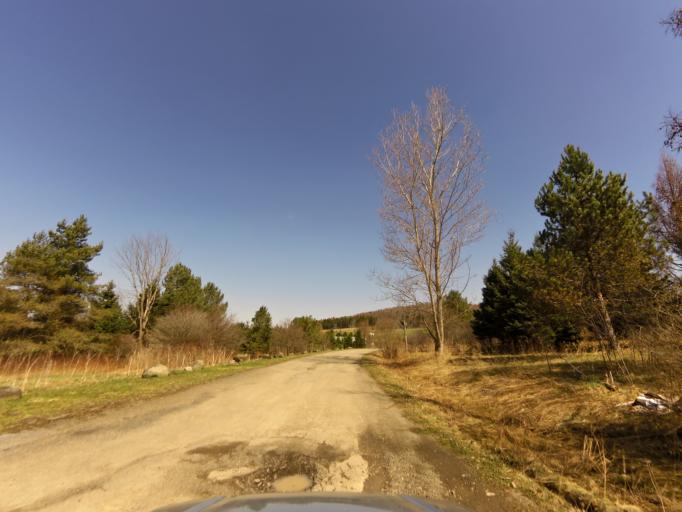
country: US
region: New York
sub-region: Cattaraugus County
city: Franklinville
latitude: 42.3216
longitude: -78.4343
